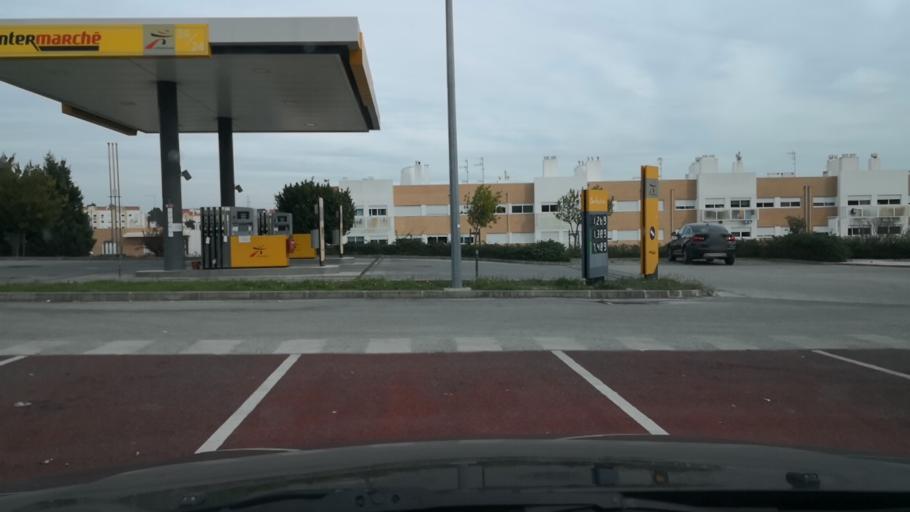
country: PT
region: Setubal
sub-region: Setubal
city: Setubal
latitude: 38.5377
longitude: -8.8569
